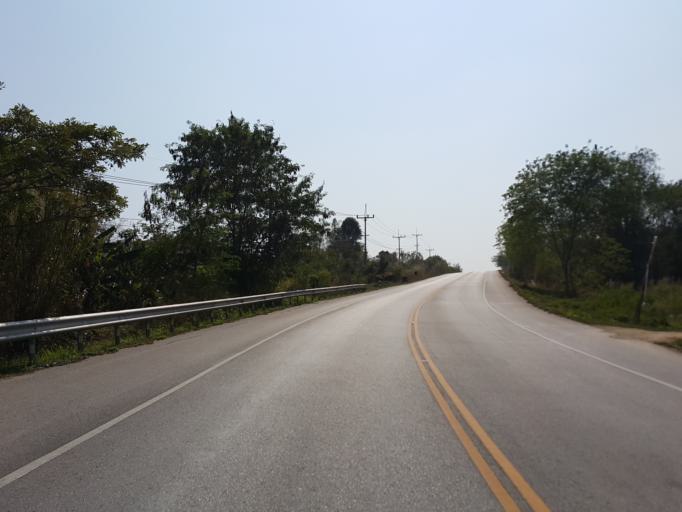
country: TH
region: Lampang
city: Wang Nuea
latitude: 18.9614
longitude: 99.6122
